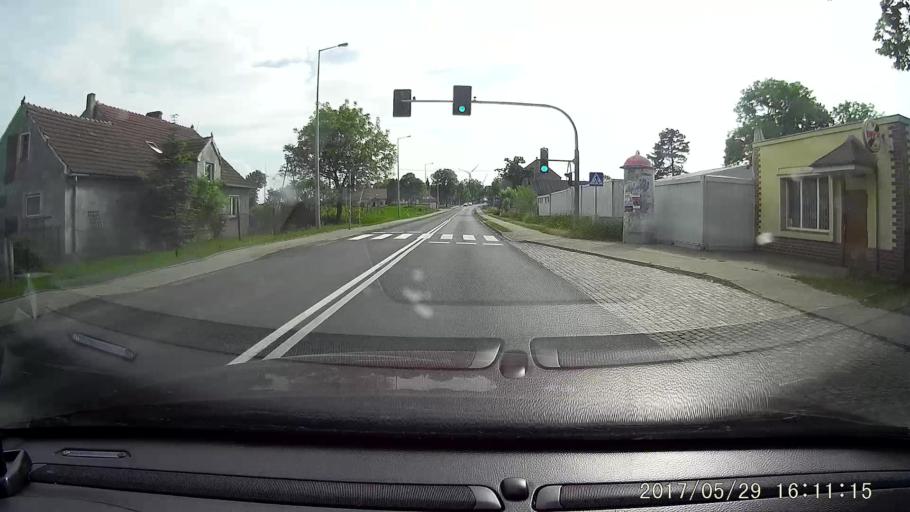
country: PL
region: Lower Silesian Voivodeship
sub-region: Powiat zgorzelecki
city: Lagow
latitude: 51.1962
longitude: 15.0856
